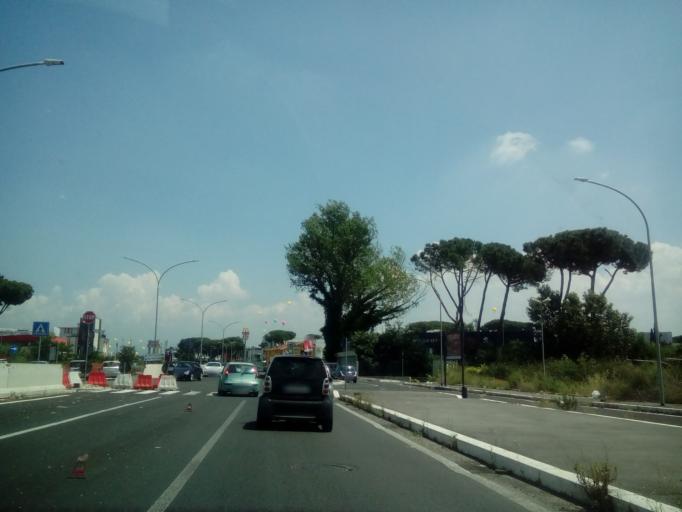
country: IT
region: Latium
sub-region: Citta metropolitana di Roma Capitale
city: Colle Verde
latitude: 41.9329
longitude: 12.5923
